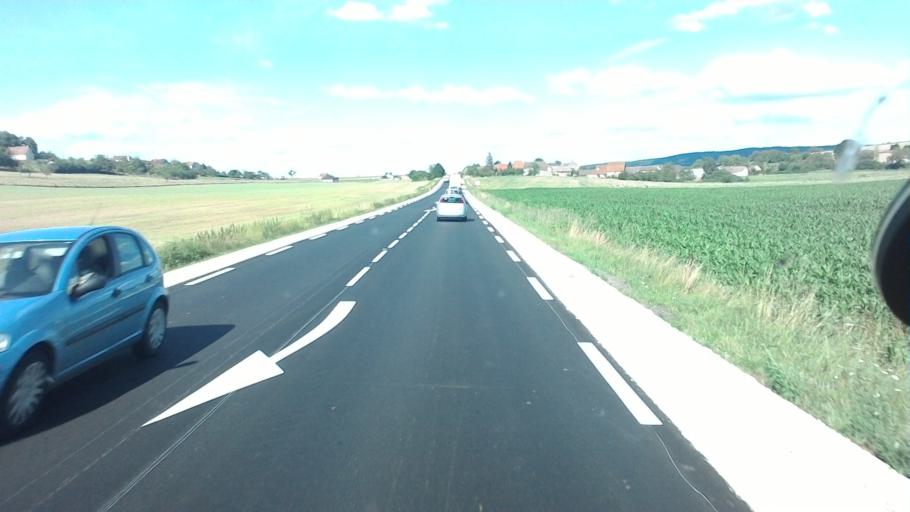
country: FR
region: Franche-Comte
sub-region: Departement de la Haute-Saone
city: Gy
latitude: 47.4275
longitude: 5.8525
